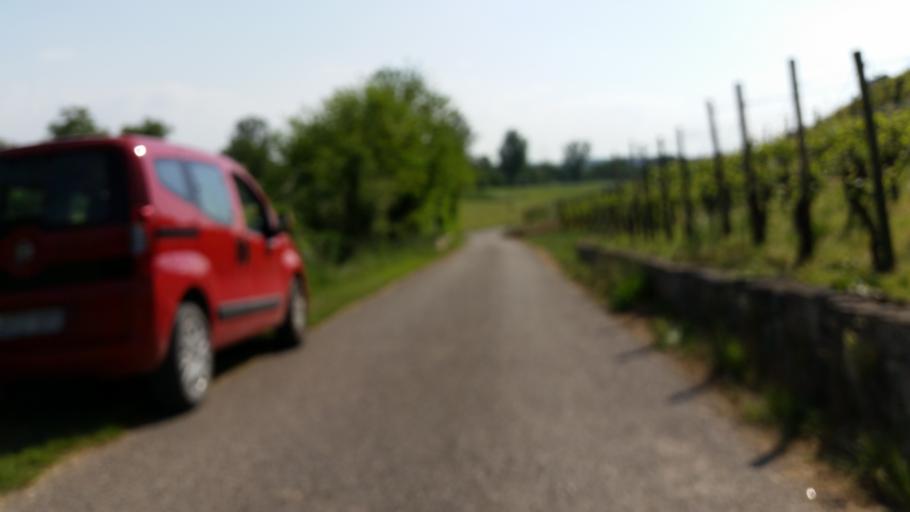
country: DE
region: Baden-Wuerttemberg
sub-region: Regierungsbezirk Stuttgart
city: Pleidelsheim
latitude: 48.9761
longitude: 9.2075
